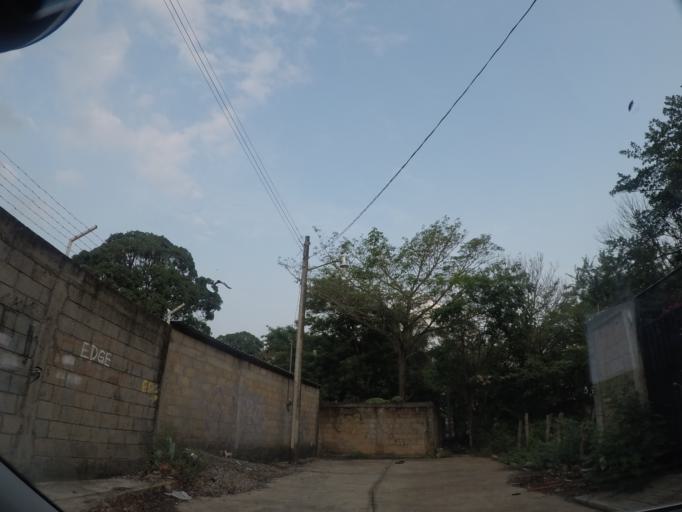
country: MX
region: Oaxaca
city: Matias Romero
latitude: 16.8707
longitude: -95.0367
